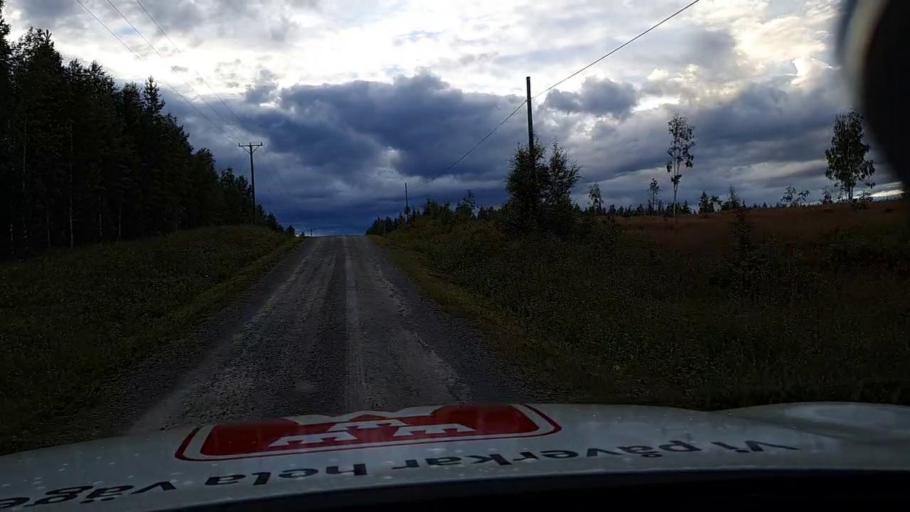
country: SE
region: Jaemtland
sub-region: Bergs Kommun
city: Hoverberg
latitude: 62.8887
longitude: 14.5712
